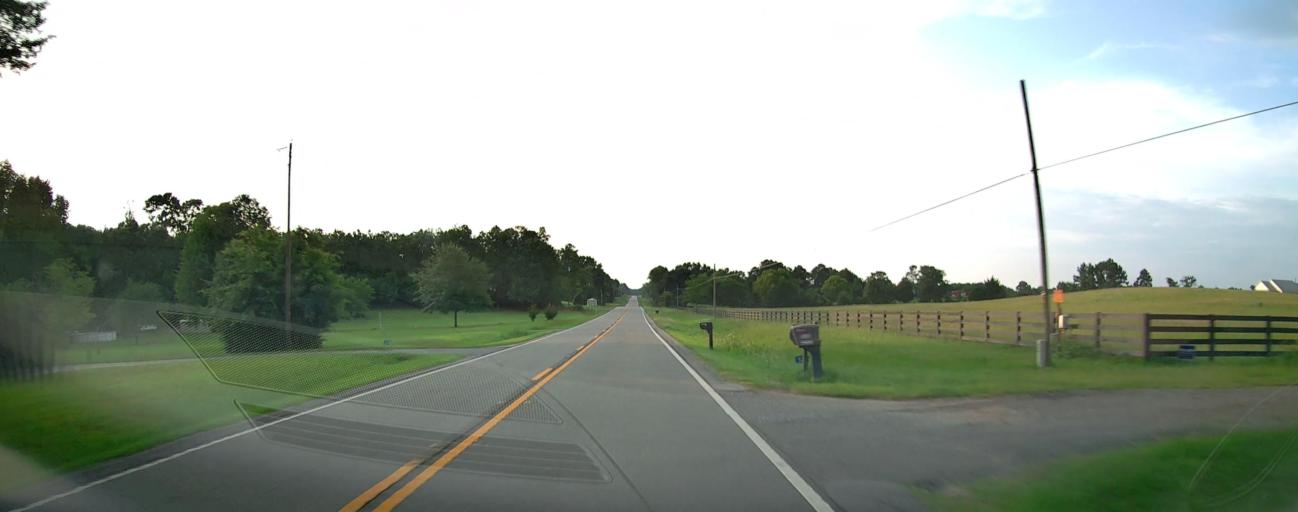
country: US
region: Georgia
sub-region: Taylor County
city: Reynolds
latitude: 32.5976
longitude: -84.0931
